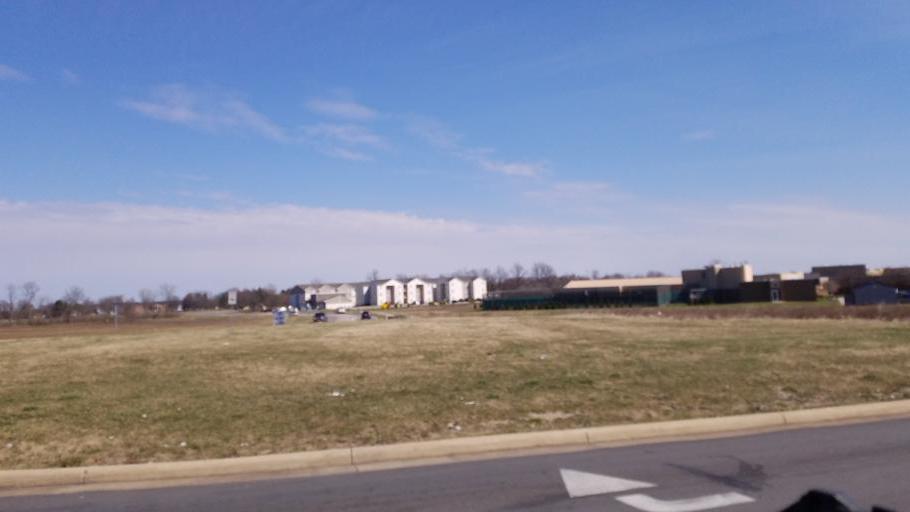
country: US
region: Ohio
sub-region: Marion County
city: Marion
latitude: 40.5822
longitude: -83.0923
